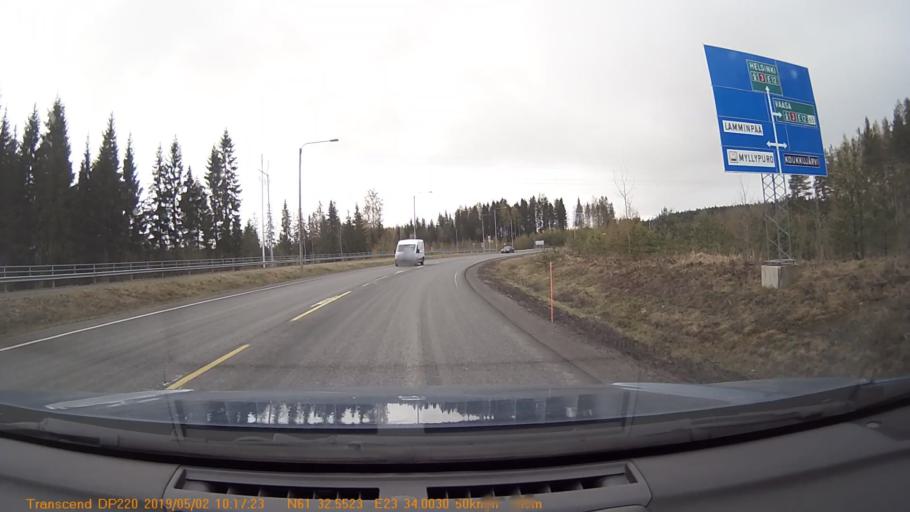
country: FI
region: Pirkanmaa
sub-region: Tampere
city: Yloejaervi
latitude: 61.5425
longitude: 23.5667
